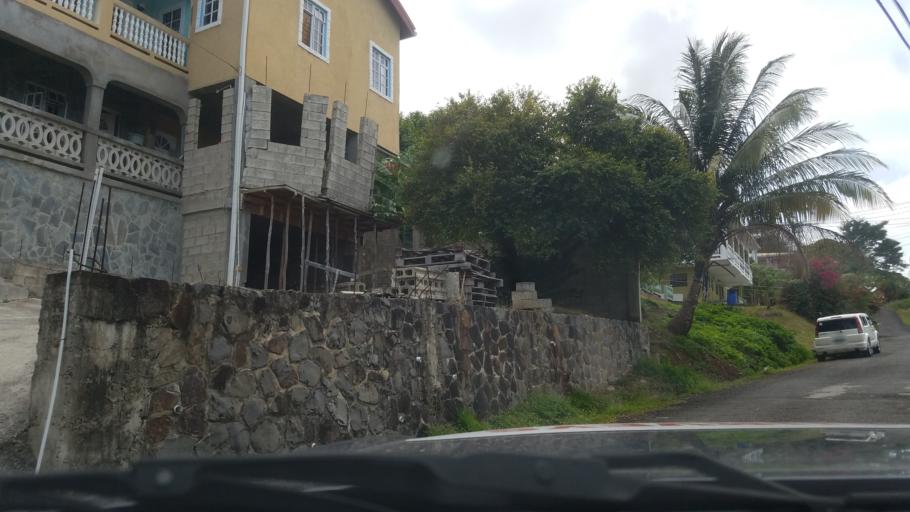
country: LC
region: Gros-Islet
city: Gros Islet
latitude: 14.0471
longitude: -60.9601
